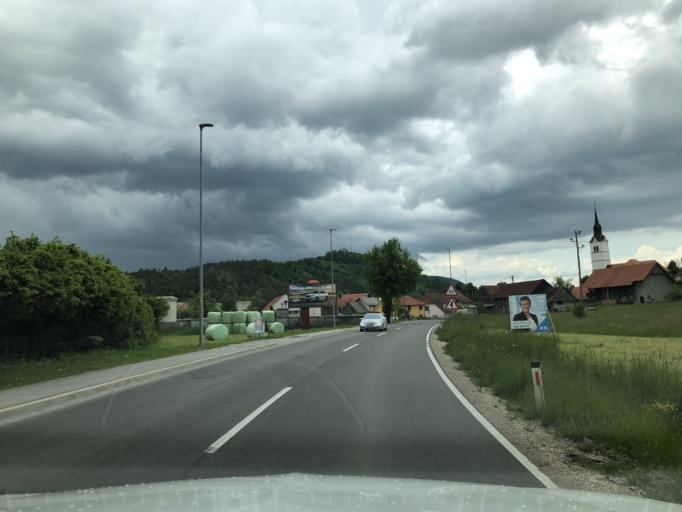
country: SI
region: Cerknica
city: Rakek
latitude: 45.8182
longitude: 14.2928
